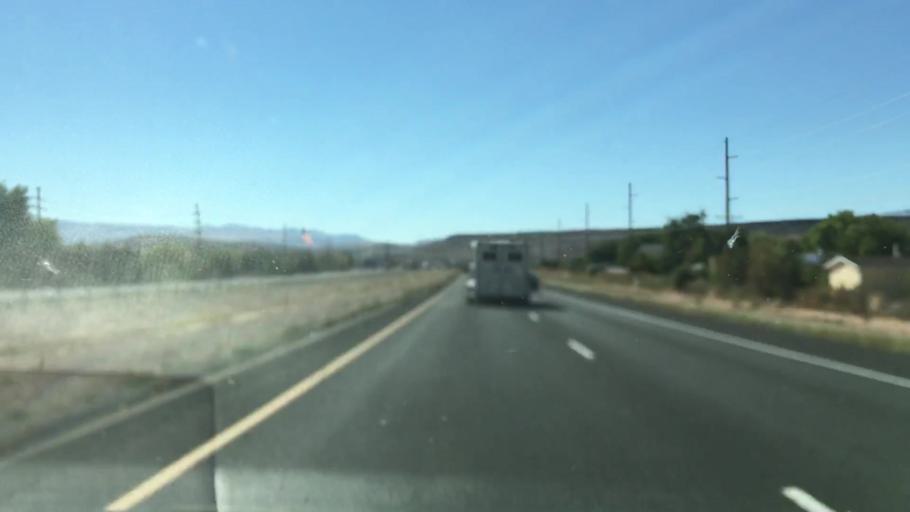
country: US
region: Utah
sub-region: Washington County
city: Saint George
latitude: 37.0931
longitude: -113.5699
